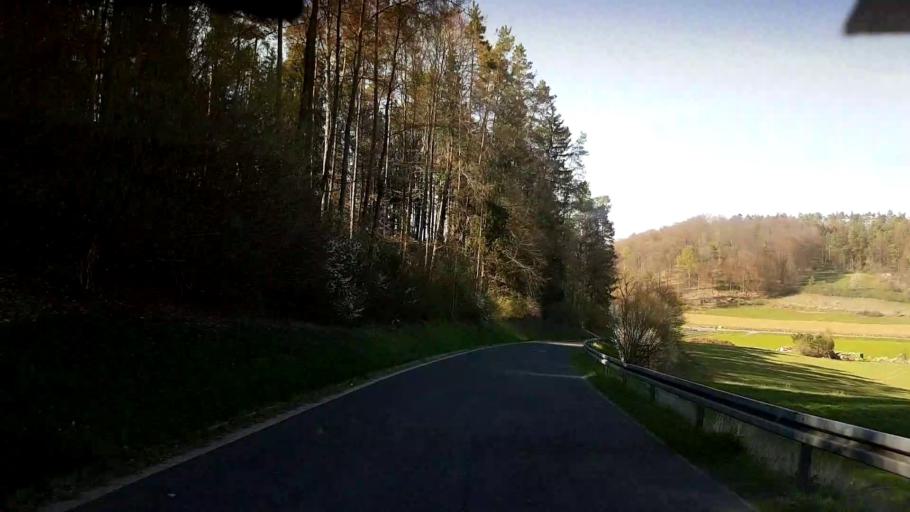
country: DE
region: Bavaria
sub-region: Upper Franconia
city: Waischenfeld
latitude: 49.8349
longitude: 11.3508
